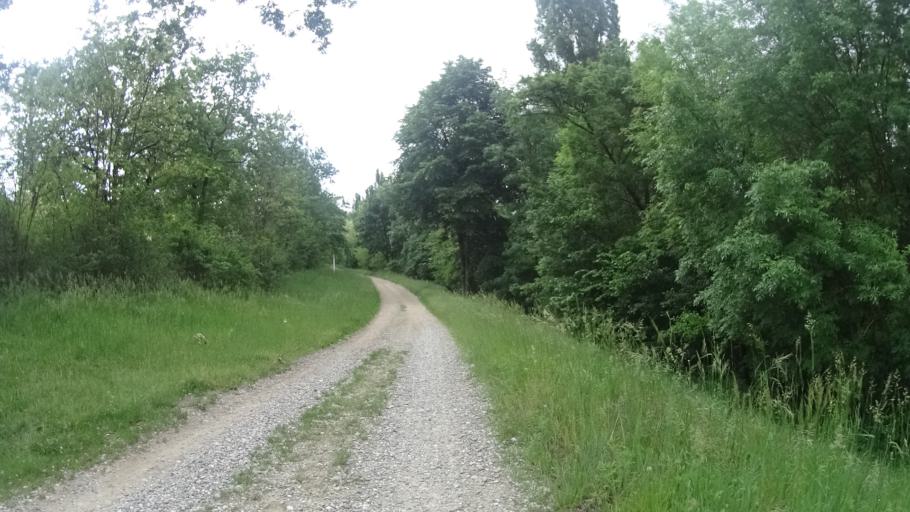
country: FR
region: Alsace
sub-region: Departement du Haut-Rhin
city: Kembs
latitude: 47.6953
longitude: 7.5137
